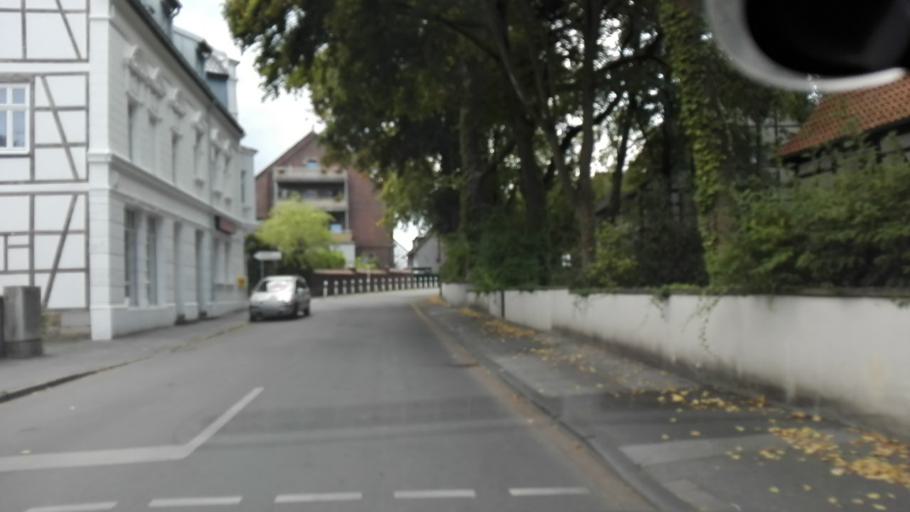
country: DE
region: North Rhine-Westphalia
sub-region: Regierungsbezirk Arnsberg
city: Dortmund
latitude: 51.4890
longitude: 7.4208
